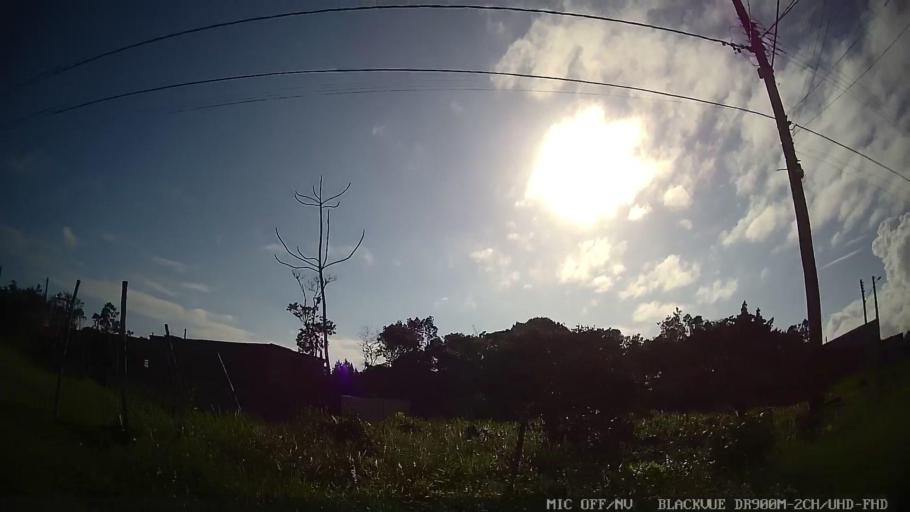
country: BR
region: Sao Paulo
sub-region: Itanhaem
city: Itanhaem
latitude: -24.2142
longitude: -46.8779
